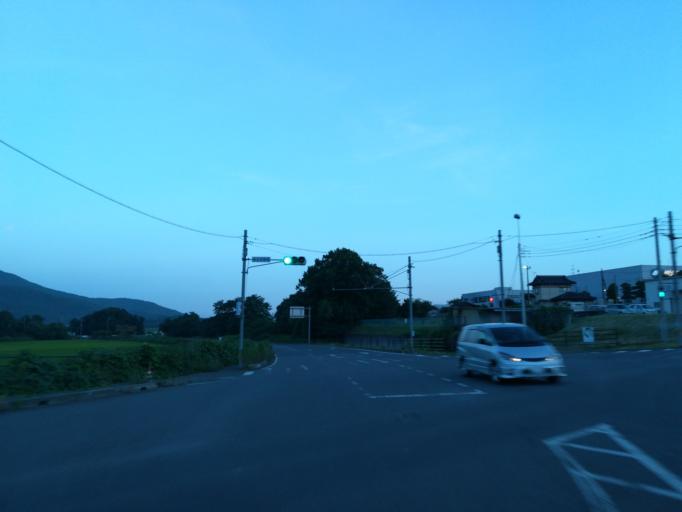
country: JP
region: Ibaraki
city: Makabe
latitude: 36.2641
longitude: 140.0586
